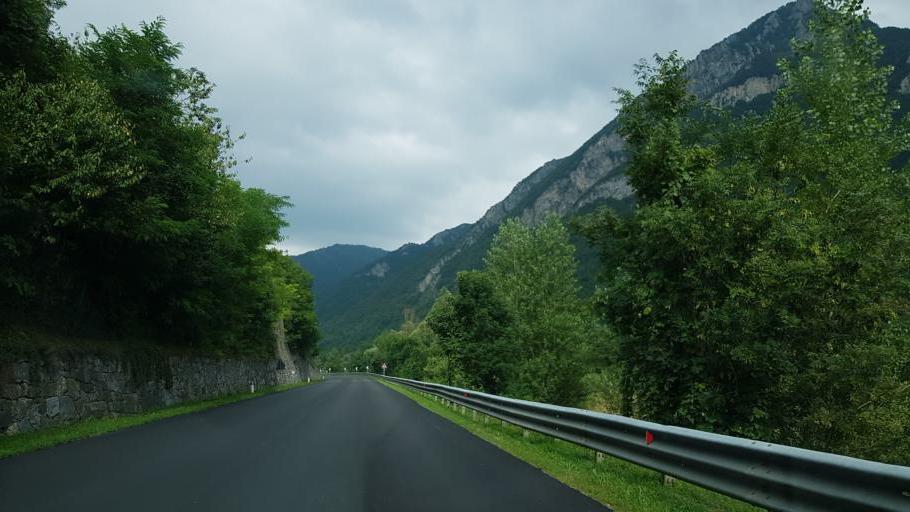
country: IT
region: Piedmont
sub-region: Provincia di Cuneo
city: Moiola
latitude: 44.3133
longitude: 7.3805
